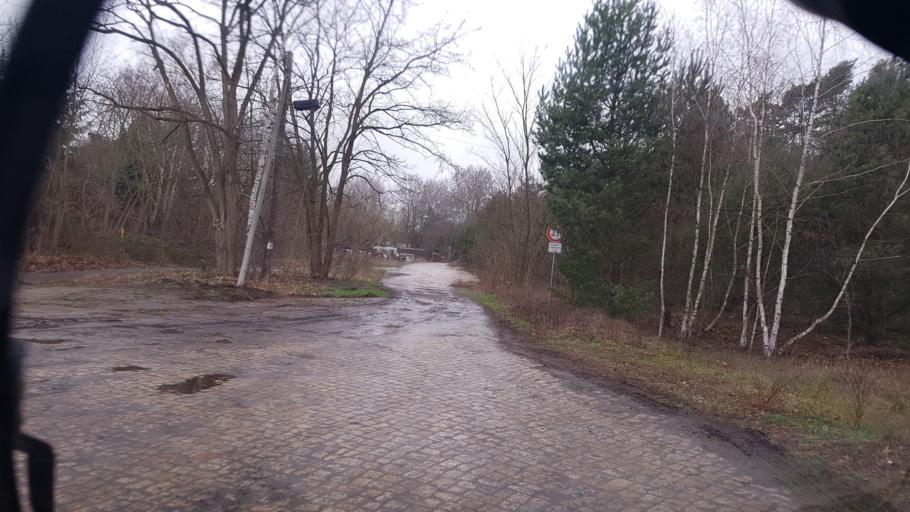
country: DE
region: Brandenburg
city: Crinitz
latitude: 51.7424
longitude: 13.7726
